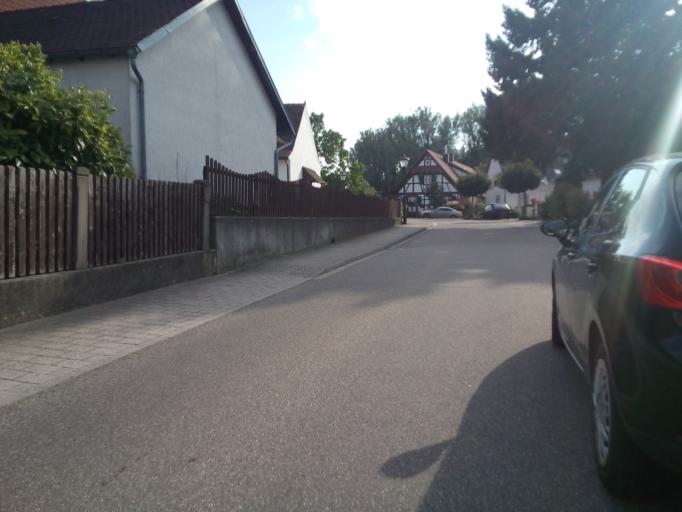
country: DE
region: Baden-Wuerttemberg
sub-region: Freiburg Region
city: Rheinau
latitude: 48.6782
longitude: 7.9389
